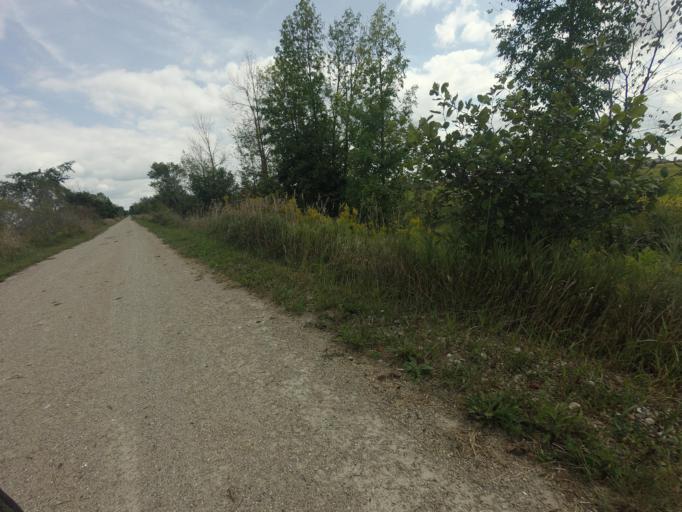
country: CA
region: Ontario
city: North Perth
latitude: 43.5715
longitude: -80.8733
